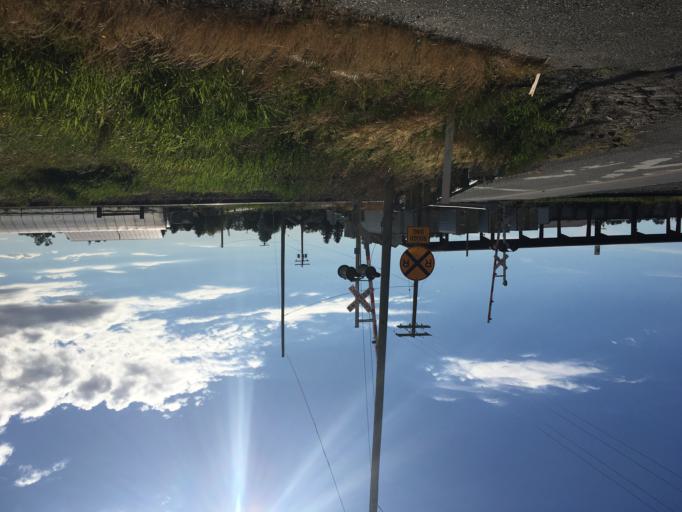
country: US
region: Washington
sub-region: Whatcom County
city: Nooksack
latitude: 48.9058
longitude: -122.3209
